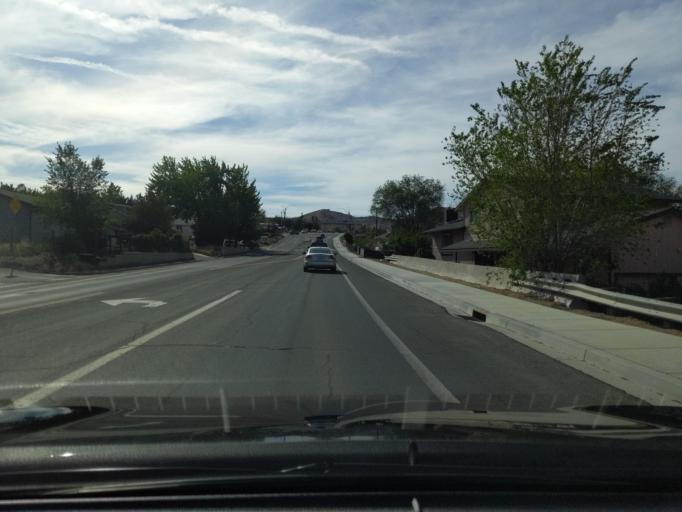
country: US
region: Nevada
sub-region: Washoe County
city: Sun Valley
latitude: 39.5662
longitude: -119.7755
